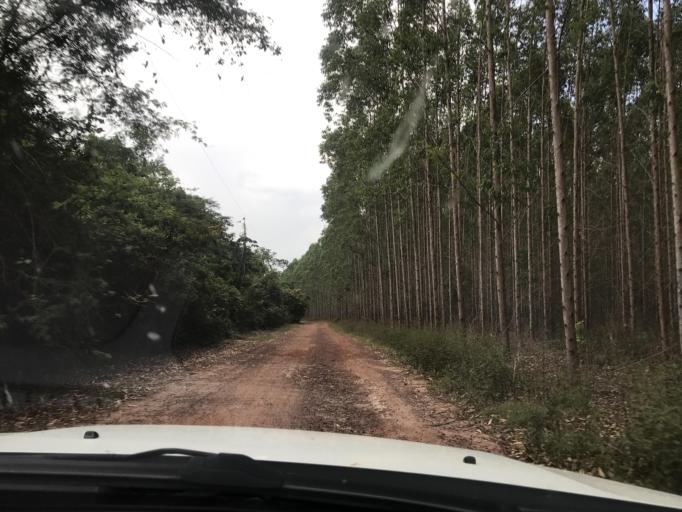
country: BR
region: Bahia
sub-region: Entre Rios
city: Entre Rios
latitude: -12.1035
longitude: -38.1880
